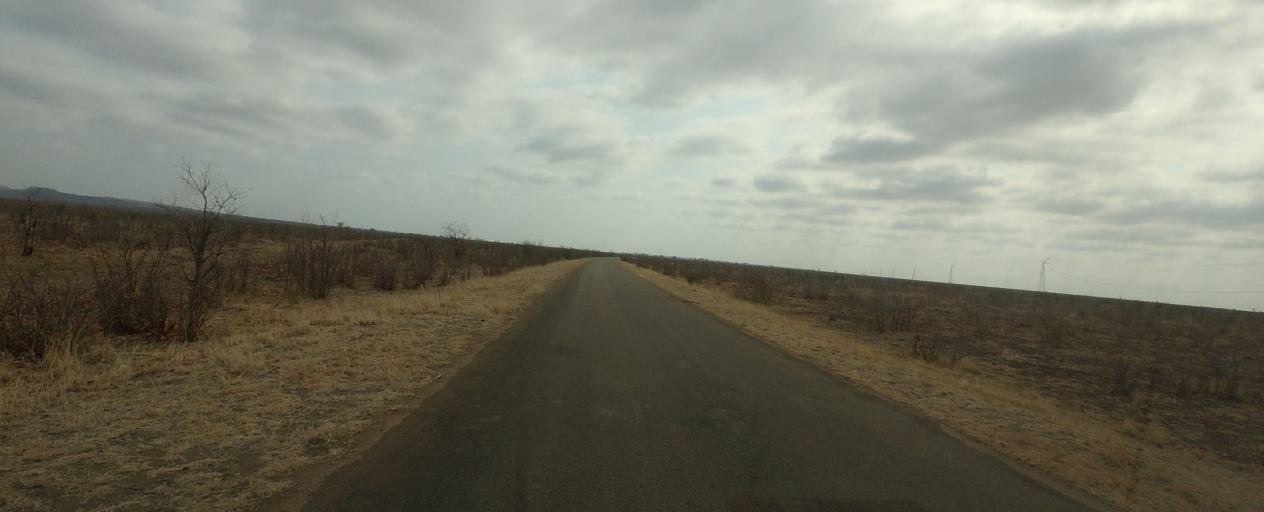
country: ZA
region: Limpopo
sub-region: Vhembe District Municipality
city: Mutale
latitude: -22.6534
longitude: 31.1711
